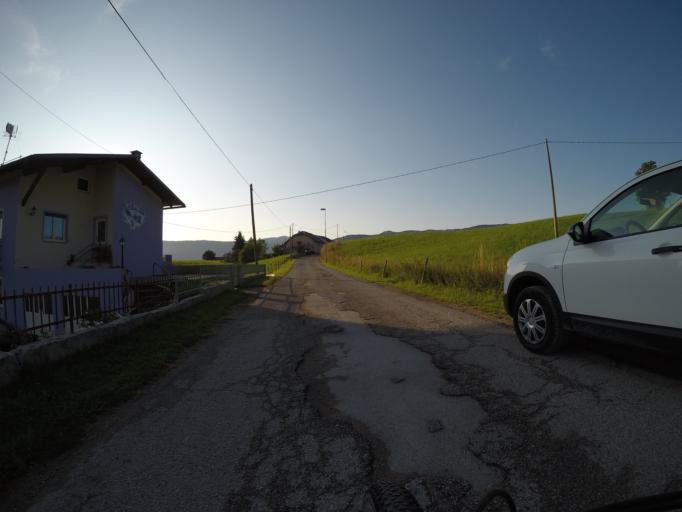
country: IT
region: Veneto
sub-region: Provincia di Vicenza
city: Asiago
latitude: 45.8618
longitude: 11.5126
